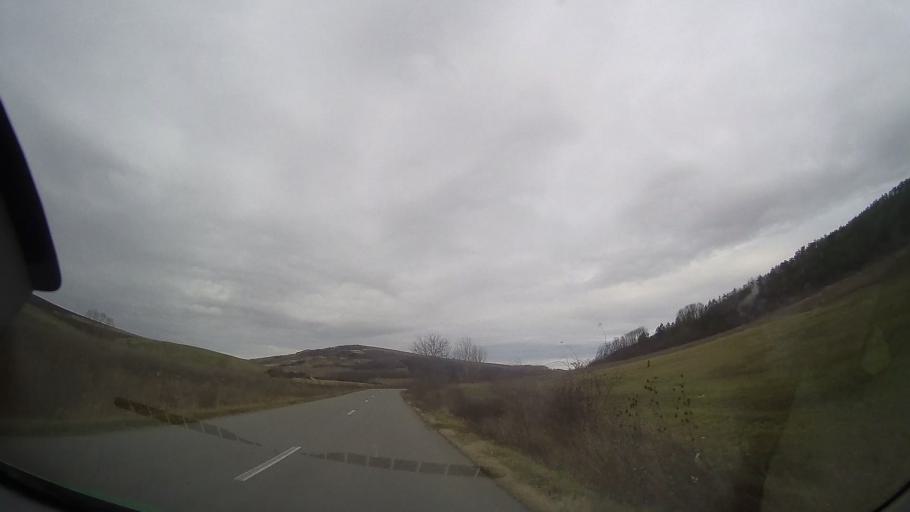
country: RO
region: Mures
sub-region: Comuna Bala
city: Bala
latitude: 46.7242
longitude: 24.5461
